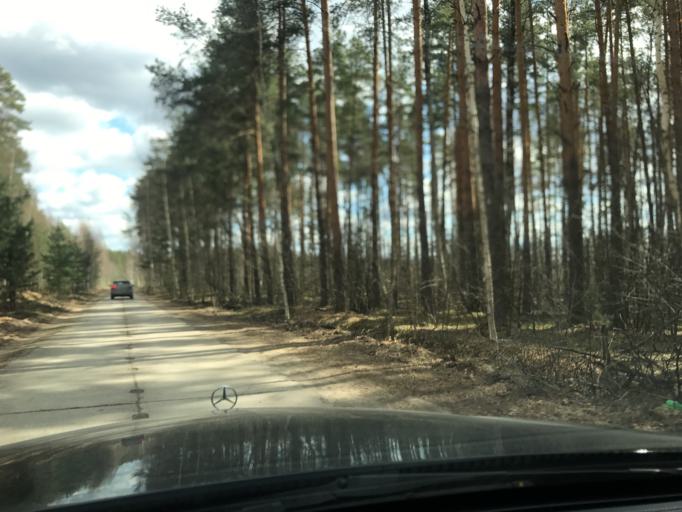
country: RU
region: Moskovskaya
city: Vereya
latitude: 55.8401
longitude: 39.0971
